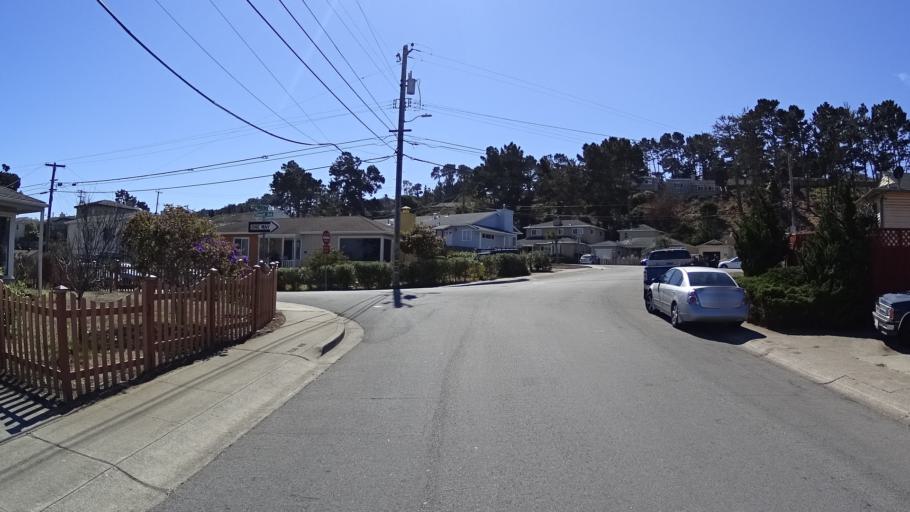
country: US
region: California
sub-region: San Mateo County
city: Broadmoor
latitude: 37.6950
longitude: -122.4852
